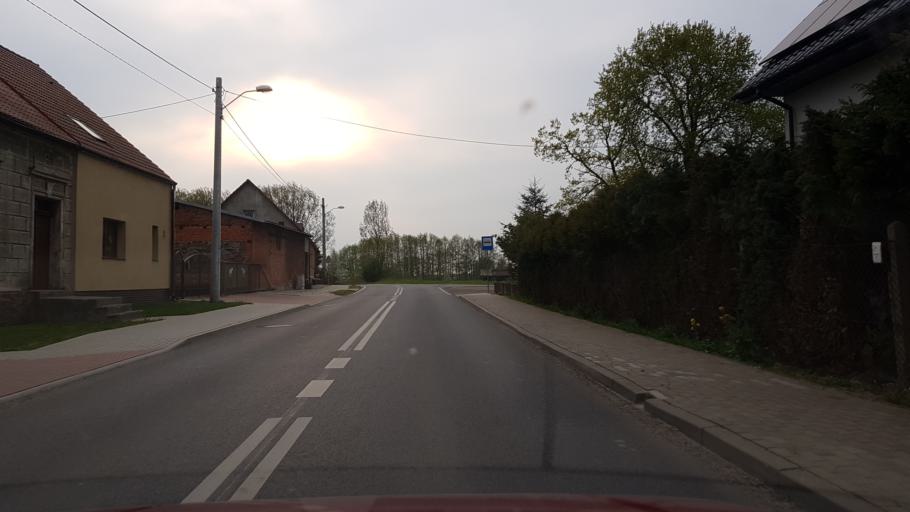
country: PL
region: West Pomeranian Voivodeship
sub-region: Powiat pyrzycki
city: Bielice
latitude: 53.2750
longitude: 14.6670
